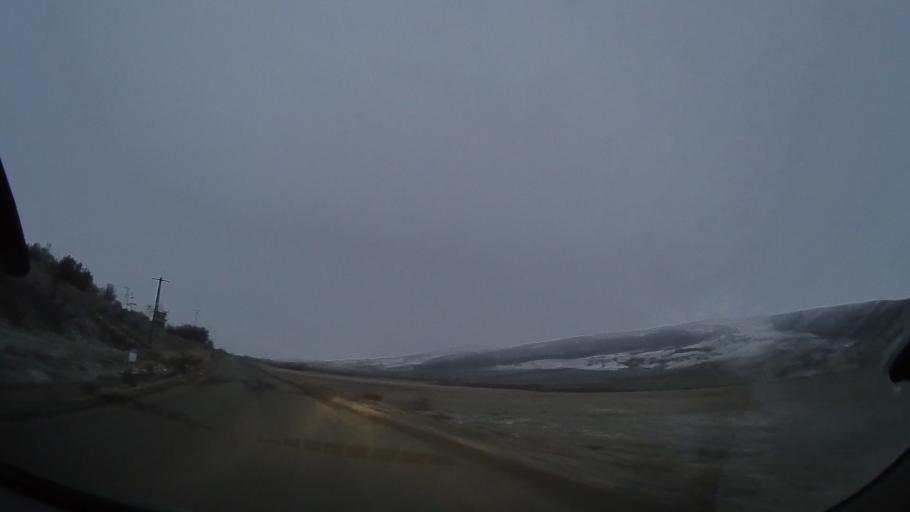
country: RO
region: Vaslui
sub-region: Comuna Vutcani
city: Vutcani
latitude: 46.4056
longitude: 27.9927
